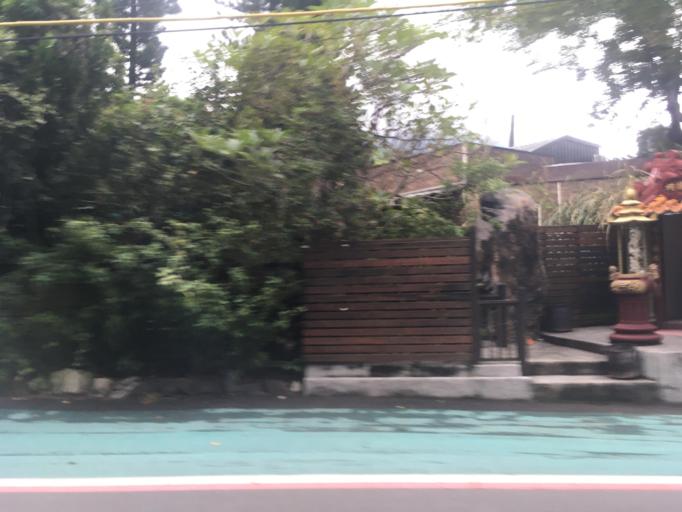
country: TW
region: Taipei
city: Taipei
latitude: 25.1400
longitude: 121.5282
